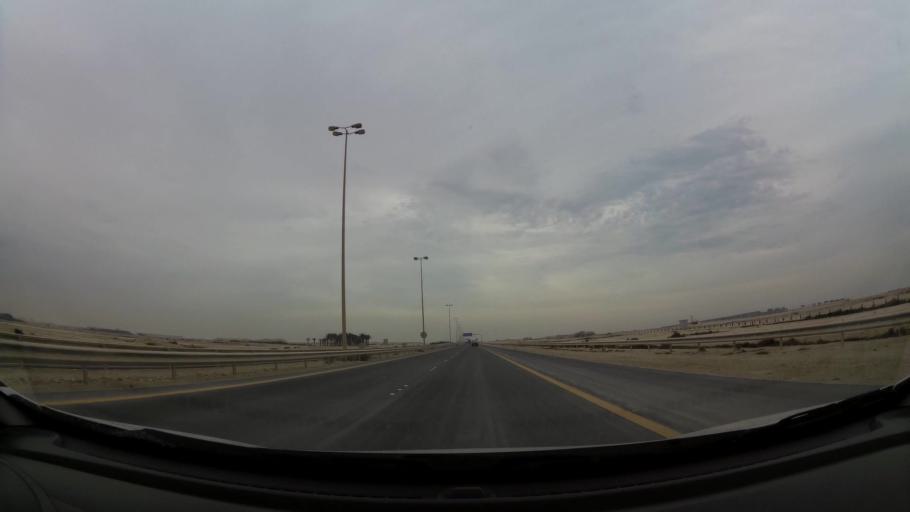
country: BH
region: Central Governorate
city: Dar Kulayb
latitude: 26.0311
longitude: 50.6078
